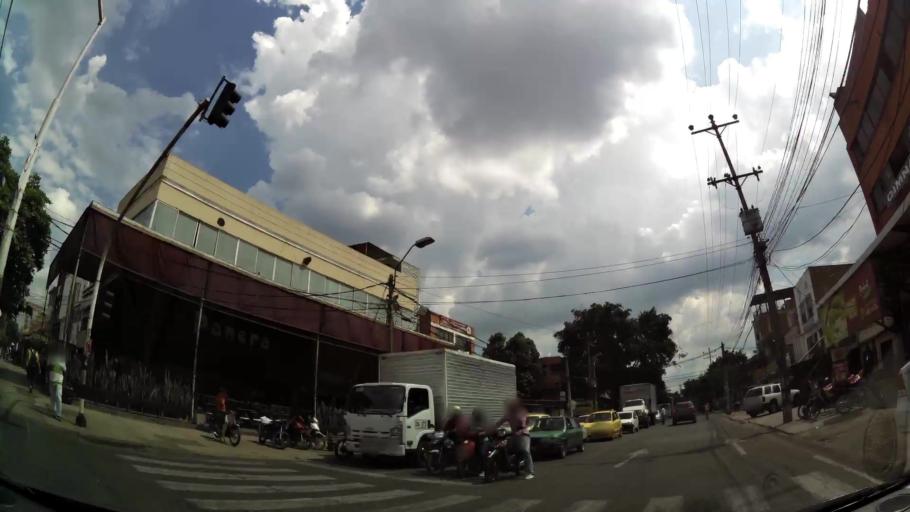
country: CO
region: Valle del Cauca
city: Cali
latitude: 3.4870
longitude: -76.5007
